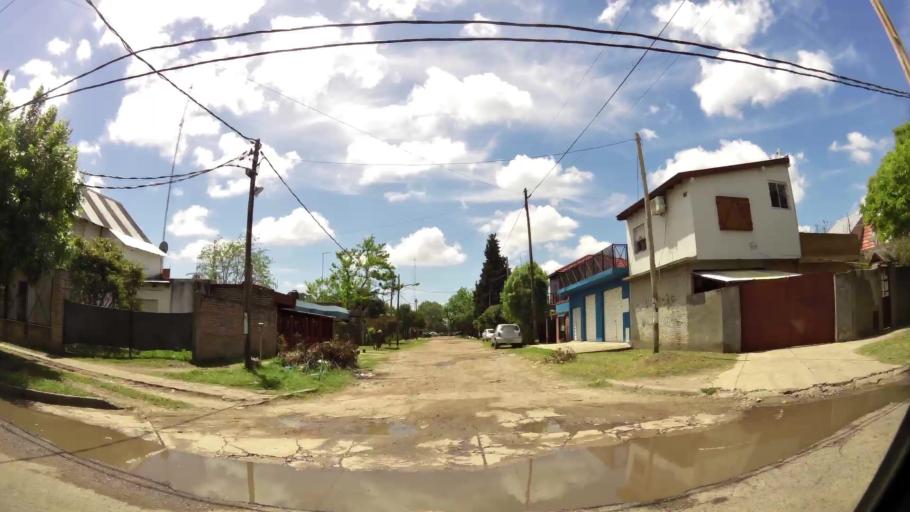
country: AR
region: Buenos Aires
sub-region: Partido de Quilmes
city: Quilmes
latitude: -34.8228
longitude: -58.2309
